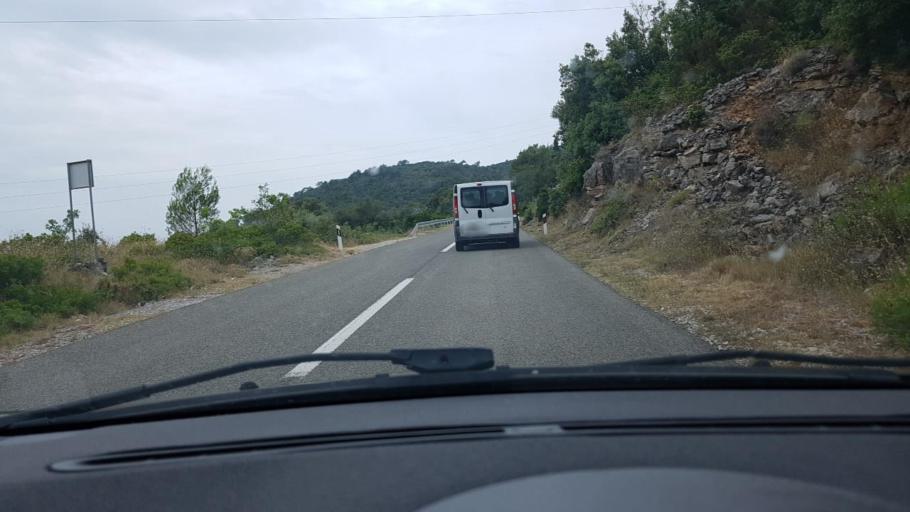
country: HR
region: Dubrovacko-Neretvanska
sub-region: Grad Korcula
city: Zrnovo
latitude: 42.9464
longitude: 17.0291
